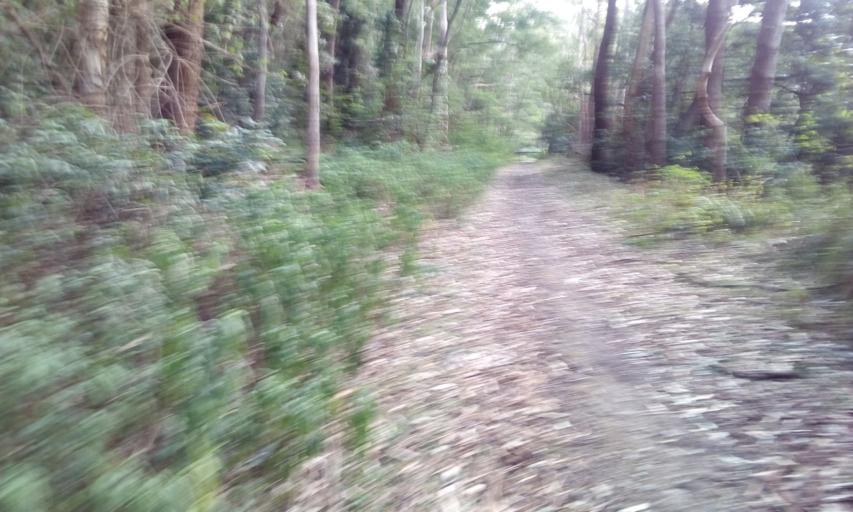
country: AU
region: New South Wales
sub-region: Wollongong
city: Cordeaux Heights
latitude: -34.4382
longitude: 150.8119
